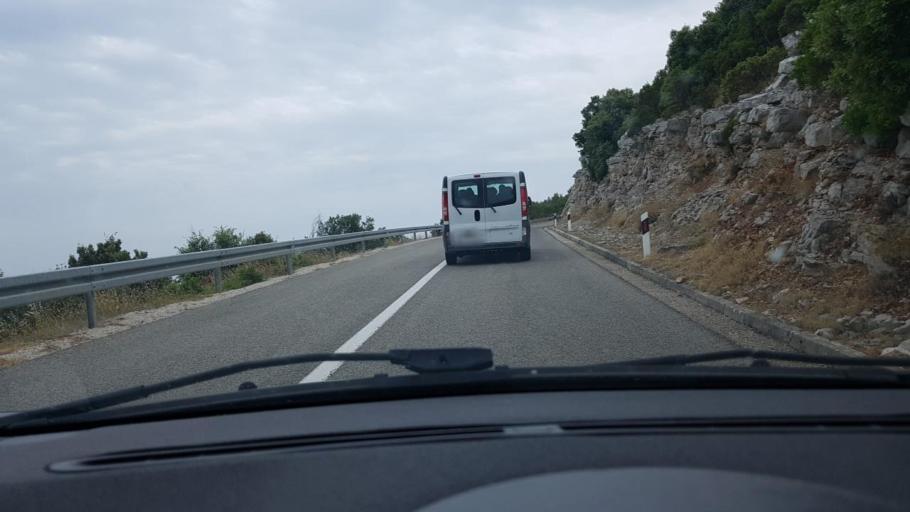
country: HR
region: Dubrovacko-Neretvanska
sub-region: Grad Korcula
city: Zrnovo
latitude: 42.9409
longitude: 17.0246
